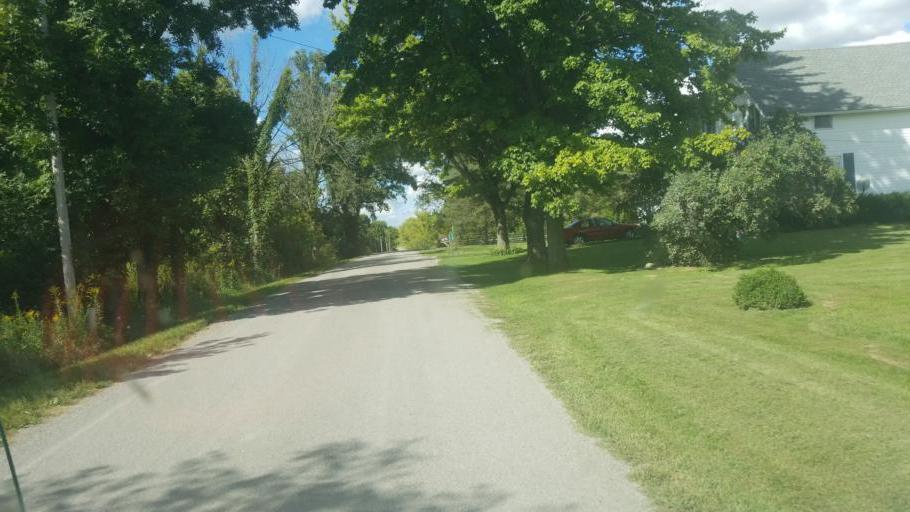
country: US
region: Ohio
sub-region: Hardin County
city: Kenton
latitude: 40.5366
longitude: -83.5429
